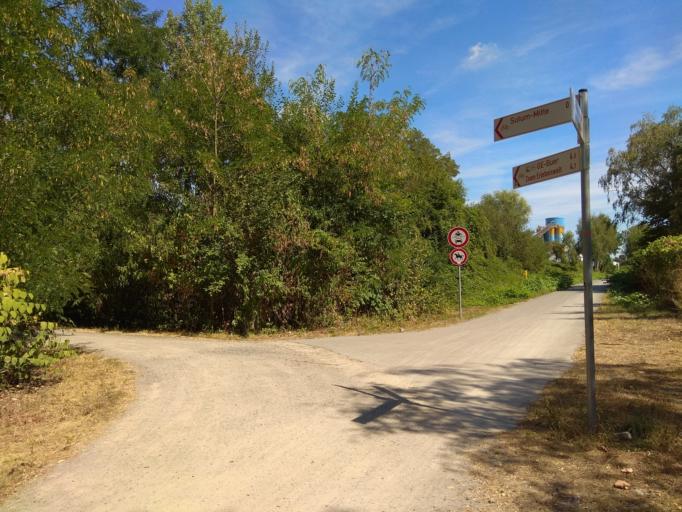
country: DE
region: North Rhine-Westphalia
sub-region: Regierungsbezirk Munster
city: Gladbeck
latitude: 51.5435
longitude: 7.0552
